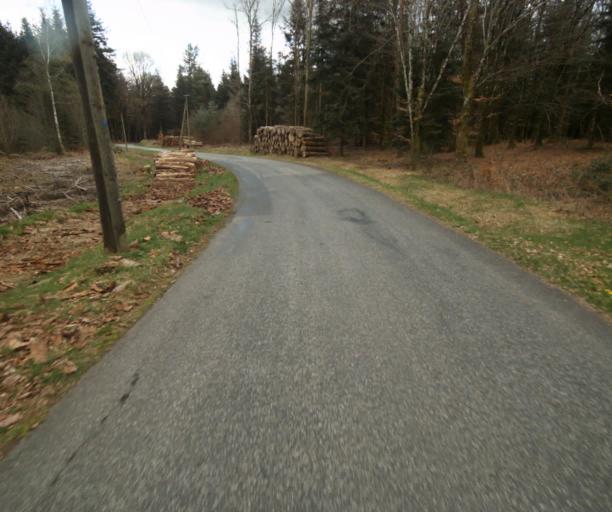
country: FR
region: Limousin
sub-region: Departement de la Correze
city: Correze
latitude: 45.2623
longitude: 1.9064
